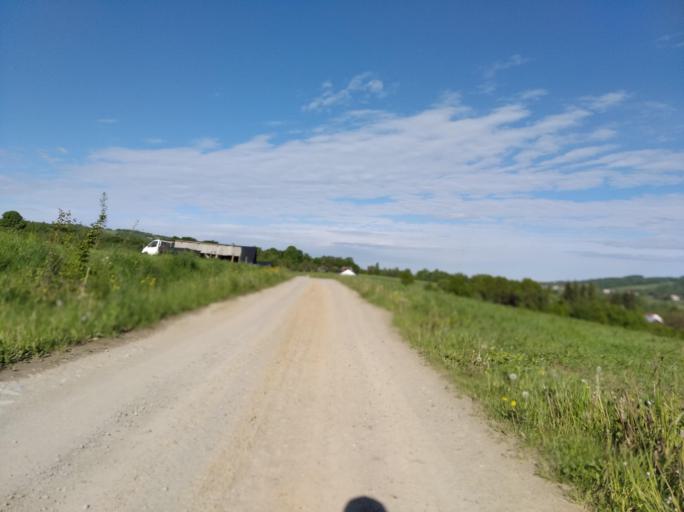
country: PL
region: Subcarpathian Voivodeship
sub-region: Powiat strzyzowski
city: Frysztak
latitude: 49.8403
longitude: 21.5693
